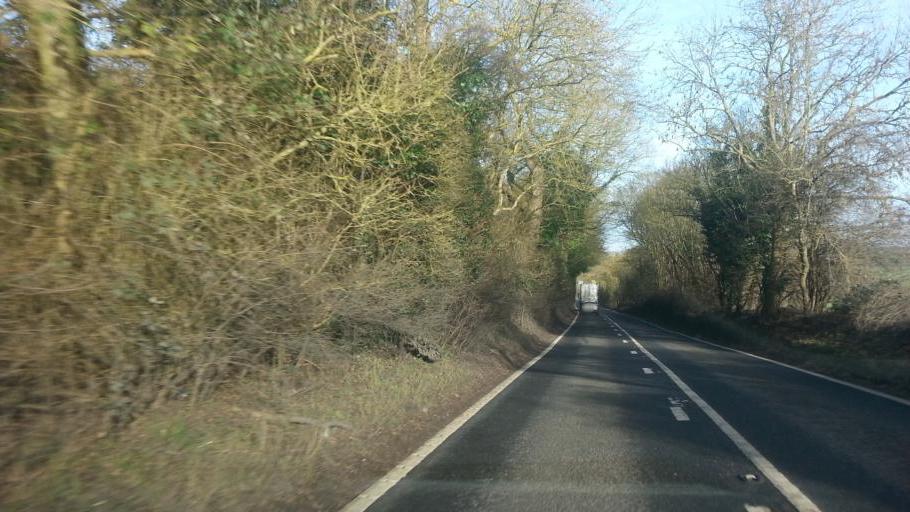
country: GB
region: England
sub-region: Cambridgeshire
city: Ramsey
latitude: 52.4218
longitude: -0.1062
